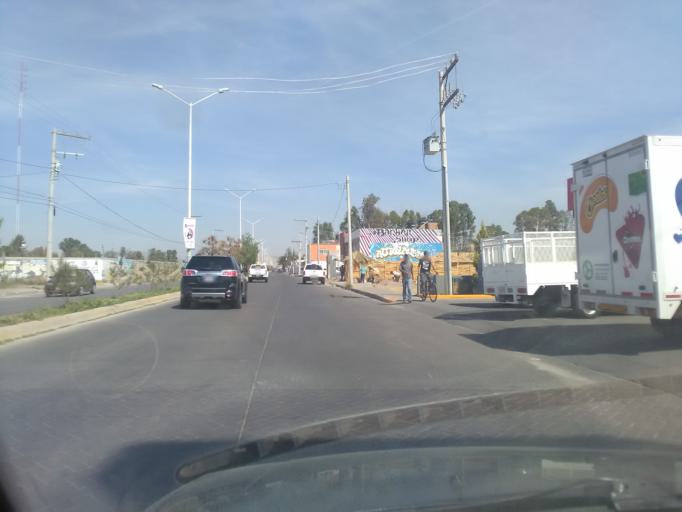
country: MX
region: Durango
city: Victoria de Durango
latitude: 24.0499
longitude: -104.6255
